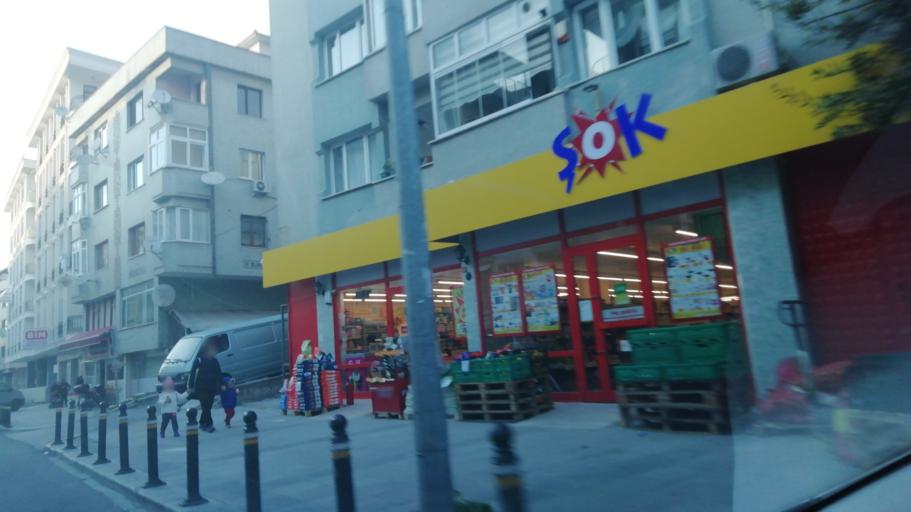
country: TR
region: Istanbul
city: Mahmutbey
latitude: 40.9933
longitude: 28.7710
